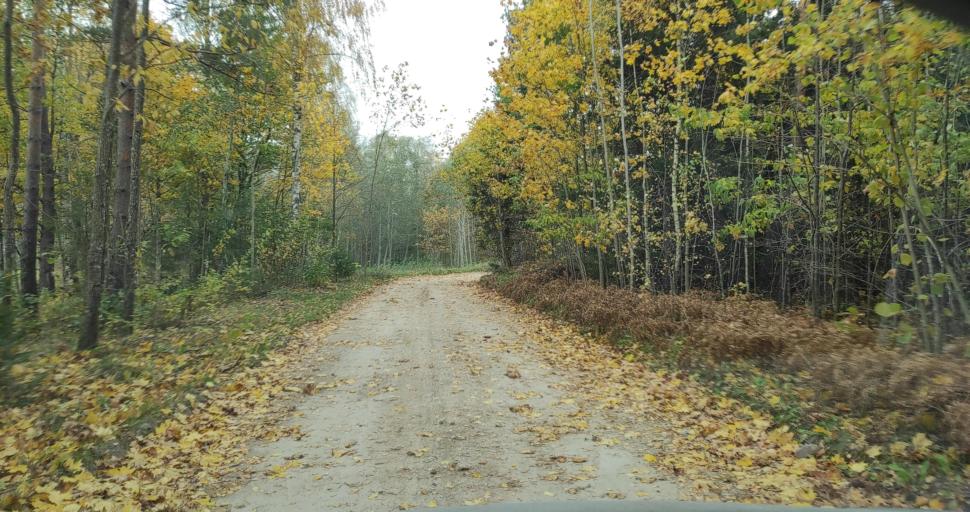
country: LV
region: Alsunga
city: Alsunga
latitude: 57.0359
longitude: 21.7126
